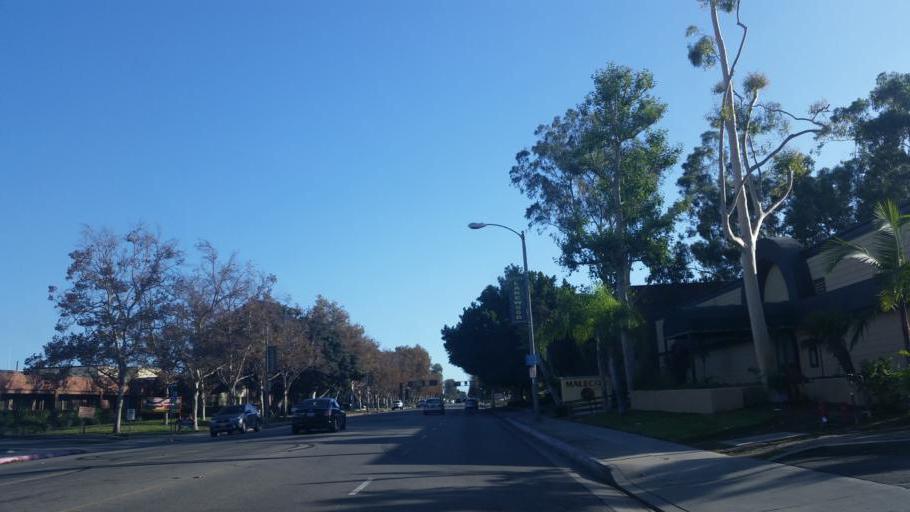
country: US
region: California
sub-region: Los Angeles County
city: Lakewood
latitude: 33.8524
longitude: -118.1339
